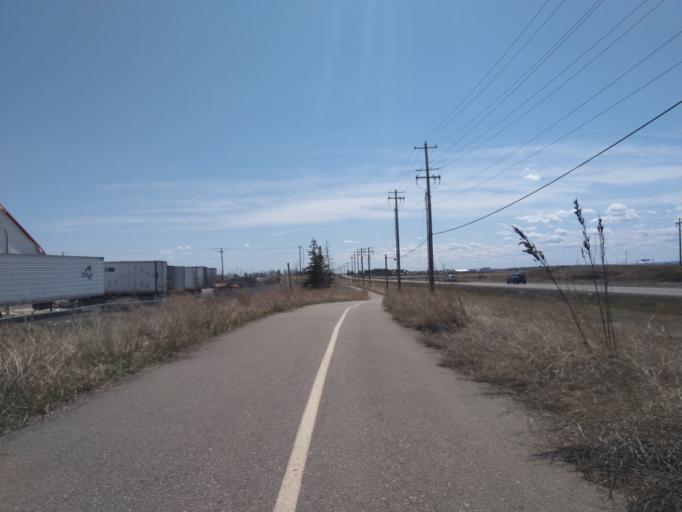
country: CA
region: Alberta
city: Chestermere
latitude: 50.9642
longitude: -113.9115
